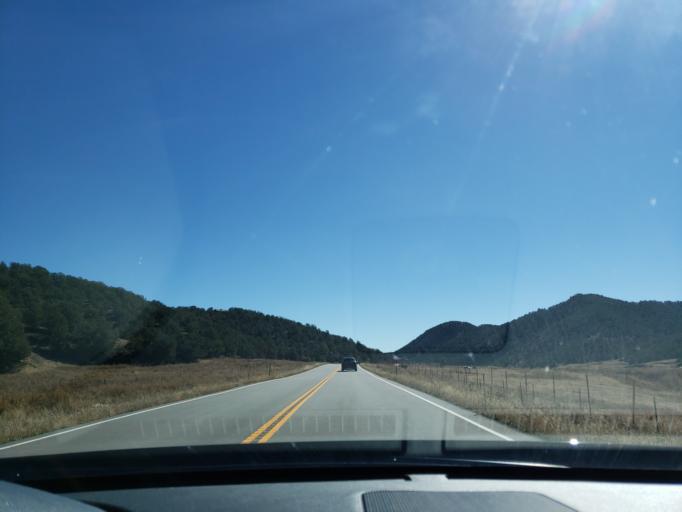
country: US
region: Colorado
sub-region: Fremont County
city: Canon City
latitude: 38.6295
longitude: -105.4603
